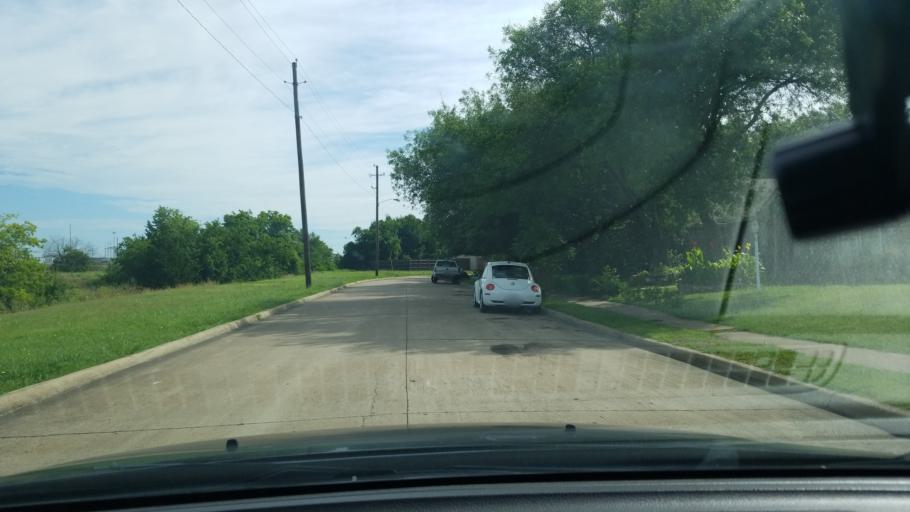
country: US
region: Texas
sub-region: Dallas County
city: Balch Springs
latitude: 32.7735
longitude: -96.6632
